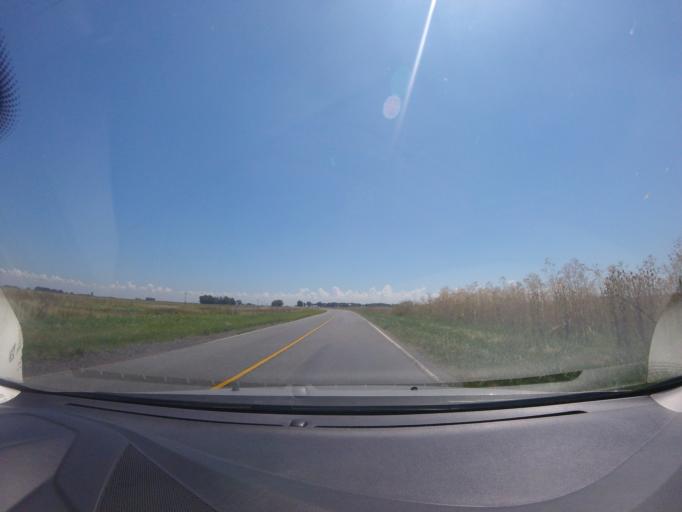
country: AR
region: Buenos Aires
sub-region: Partido de Rauch
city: Rauch
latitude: -36.4158
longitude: -58.9978
